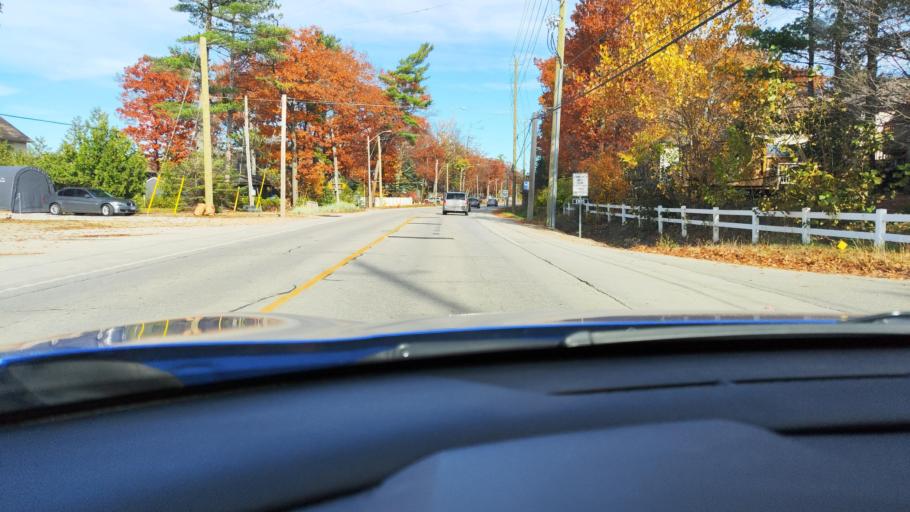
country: CA
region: Ontario
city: Wasaga Beach
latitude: 44.5135
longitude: -80.0239
